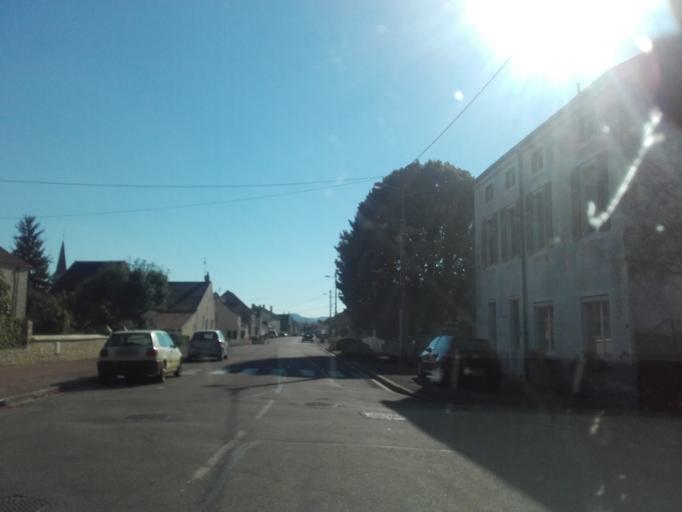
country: FR
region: Bourgogne
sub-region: Departement de la Cote-d'Or
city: Corpeau
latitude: 46.9313
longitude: 4.7536
